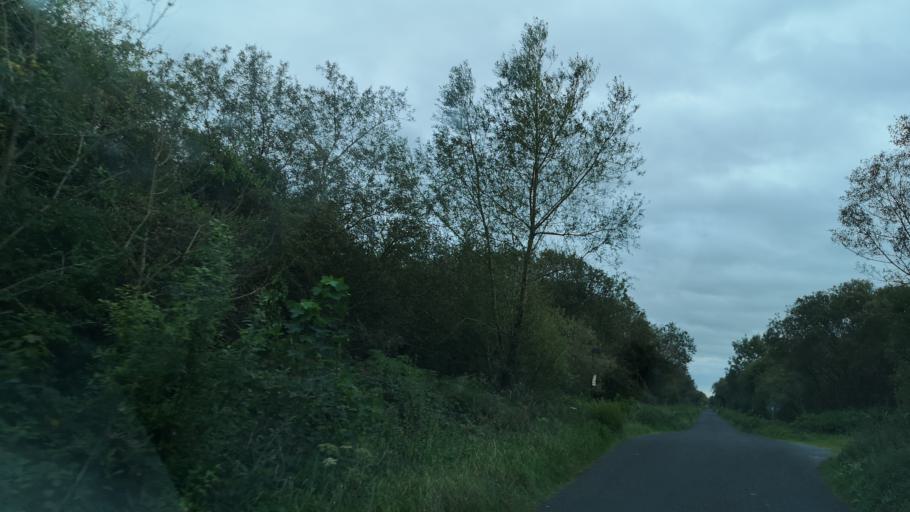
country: IE
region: Leinster
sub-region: Uibh Fhaili
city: Ferbane
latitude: 53.1969
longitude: -7.7255
